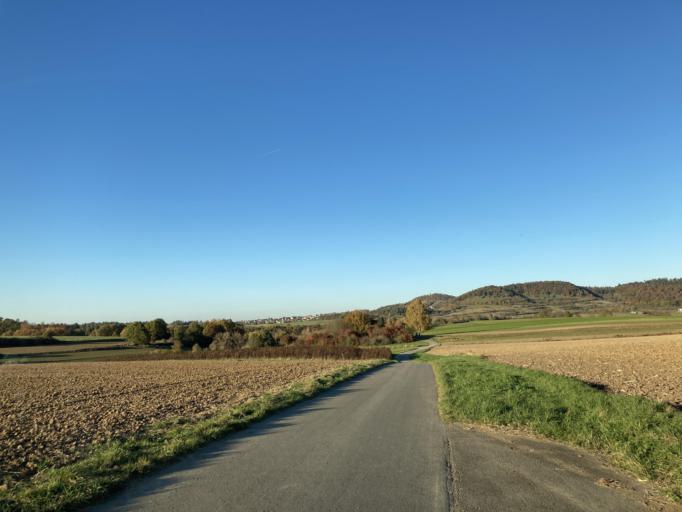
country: DE
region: Baden-Wuerttemberg
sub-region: Tuebingen Region
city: Hirrlingen
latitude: 48.4276
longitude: 8.9182
